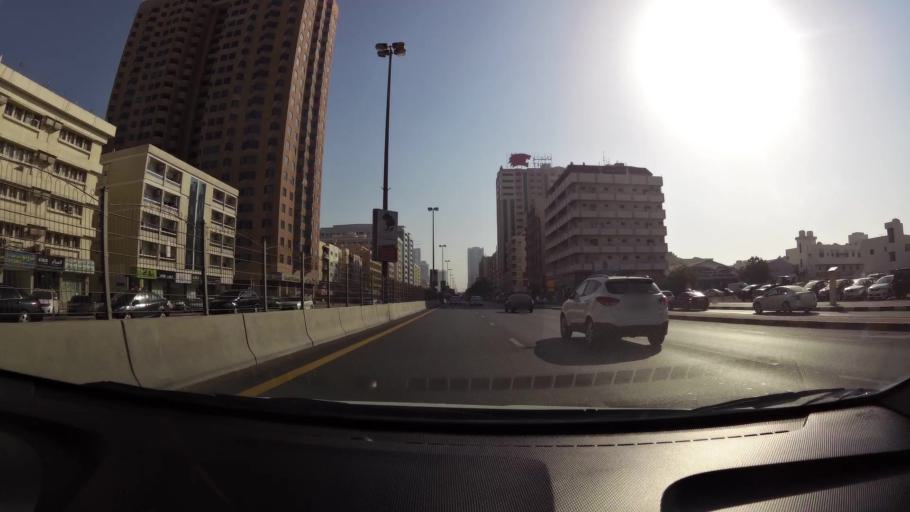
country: AE
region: Ash Shariqah
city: Sharjah
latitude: 25.3156
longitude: 55.3834
